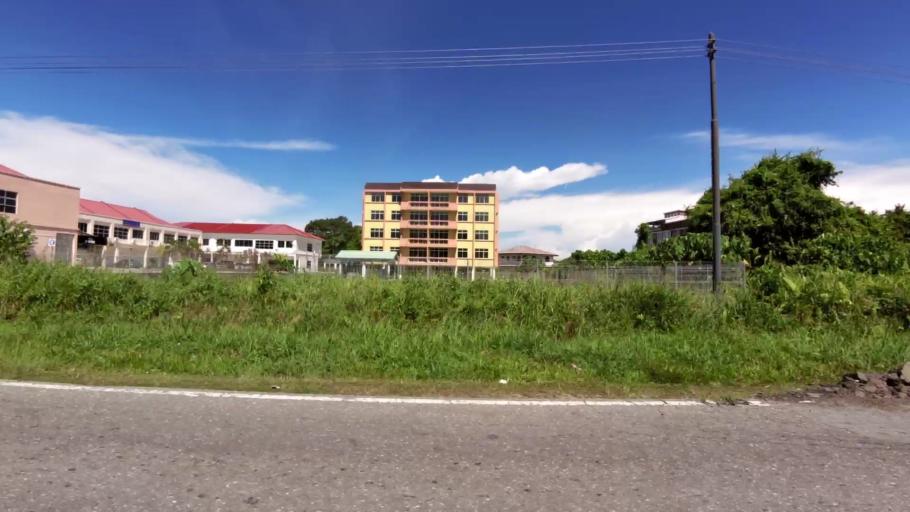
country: BN
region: Brunei and Muara
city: Bandar Seri Begawan
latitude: 5.0271
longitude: 115.0606
